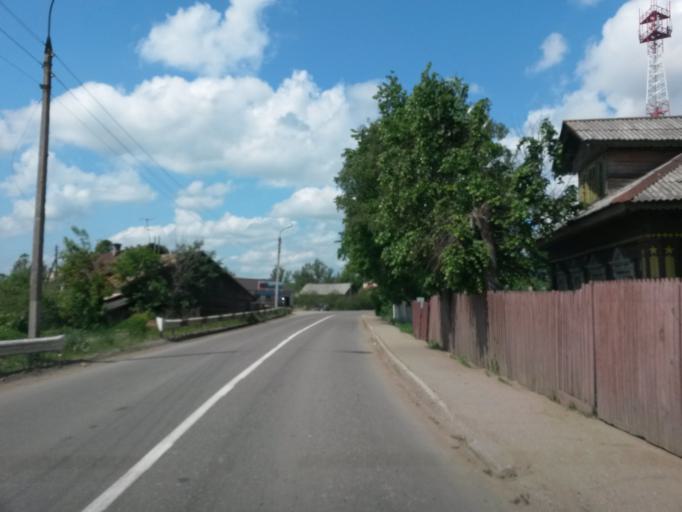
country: RU
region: Jaroslavl
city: Gavrilov-Yam
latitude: 57.3009
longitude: 39.8570
